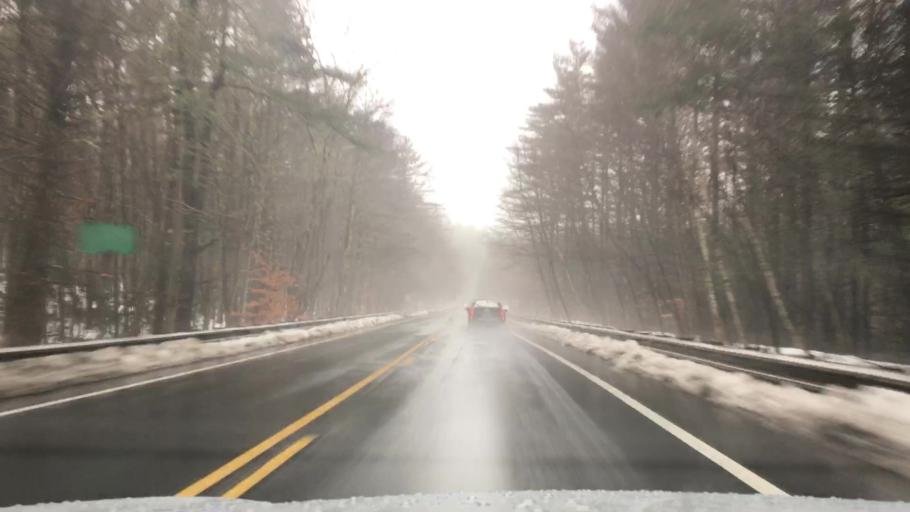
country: US
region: Massachusetts
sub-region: Franklin County
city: Shutesbury
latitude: 42.4514
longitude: -72.3864
